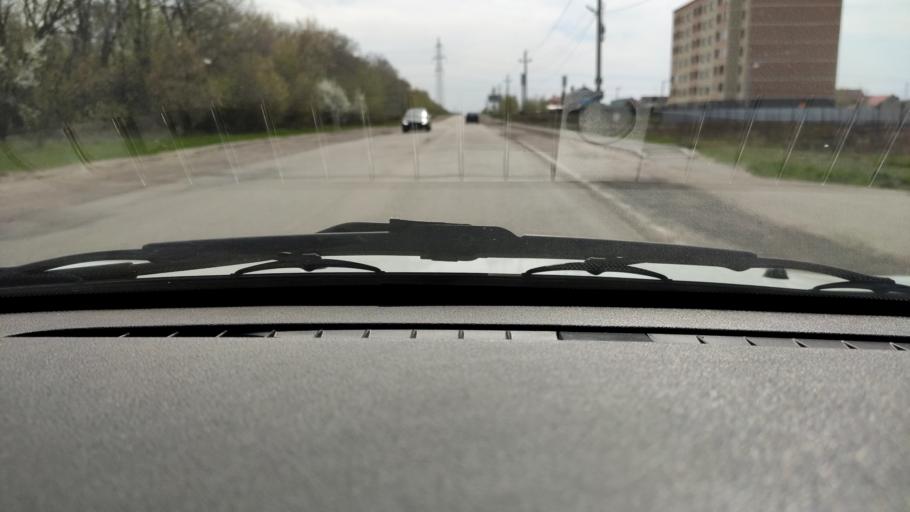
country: RU
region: Voronezj
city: Novaya Usman'
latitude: 51.6293
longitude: 39.3339
